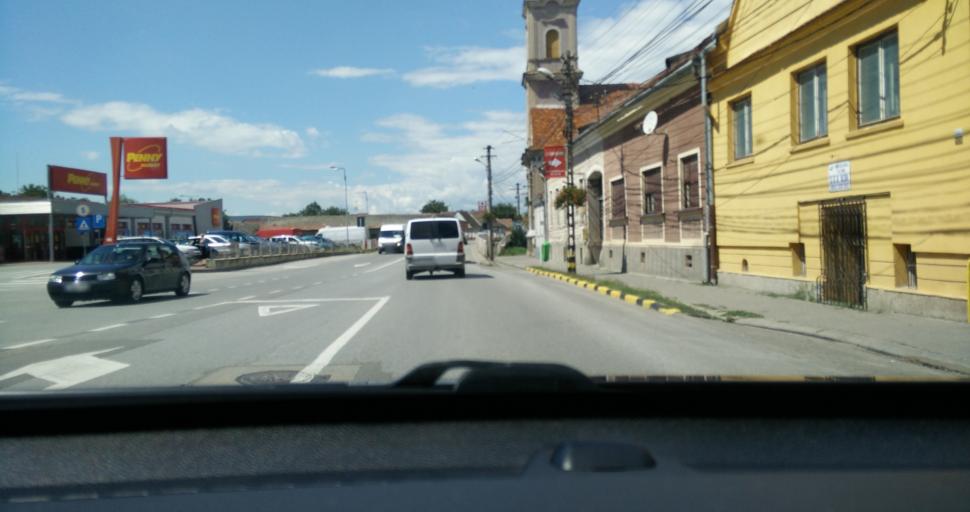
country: RO
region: Alba
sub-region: Municipiul Sebes
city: Sebes
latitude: 45.9584
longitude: 23.5635
